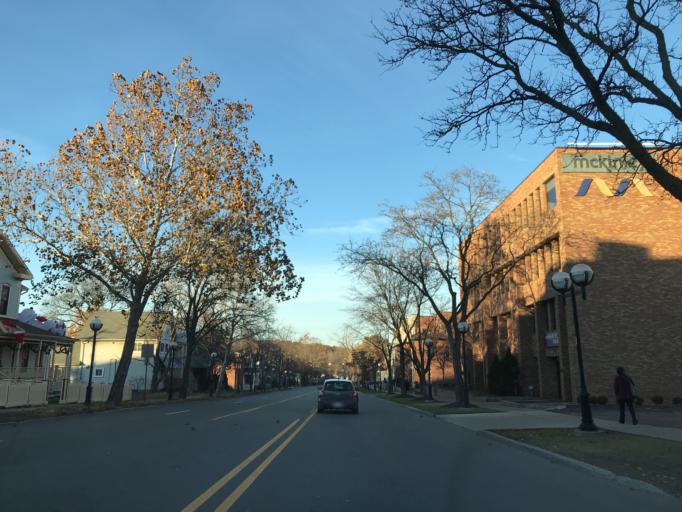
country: US
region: Michigan
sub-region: Washtenaw County
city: Ann Arbor
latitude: 42.2833
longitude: -83.7484
